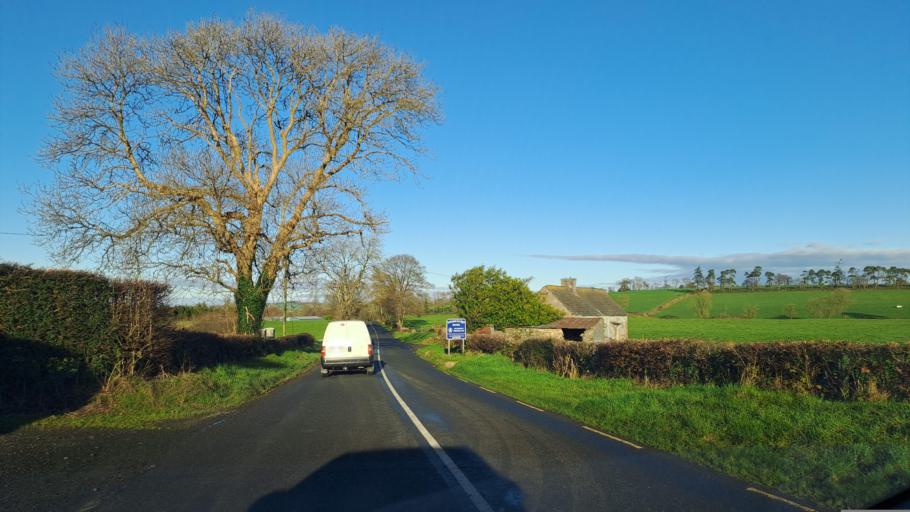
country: IE
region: Ulster
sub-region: An Cabhan
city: Mullagh
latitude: 53.8158
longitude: -6.9497
